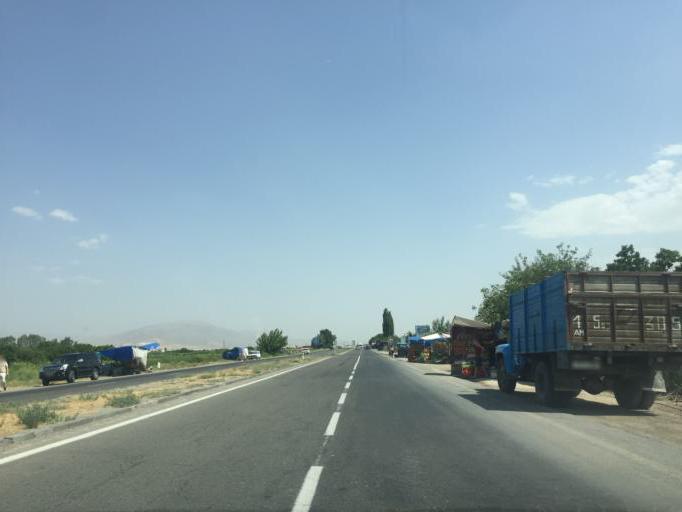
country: AM
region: Ararat
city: Shahumyan
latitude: 39.9094
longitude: 44.6034
